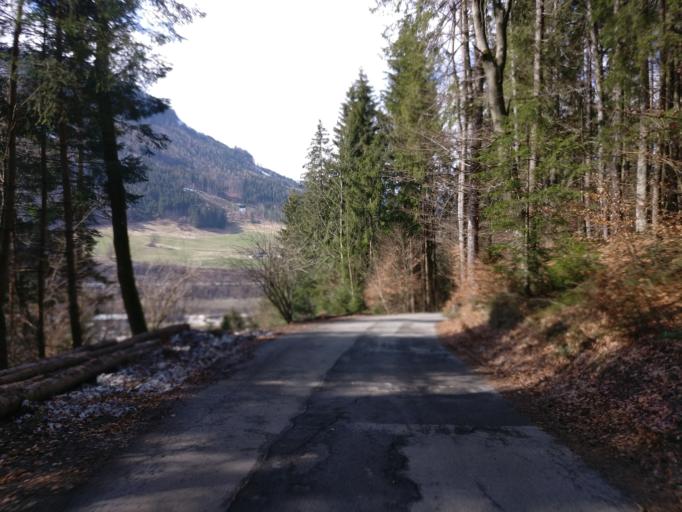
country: AT
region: Salzburg
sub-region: Politischer Bezirk Sankt Johann im Pongau
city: Bischofshofen
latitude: 47.4376
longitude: 13.2180
